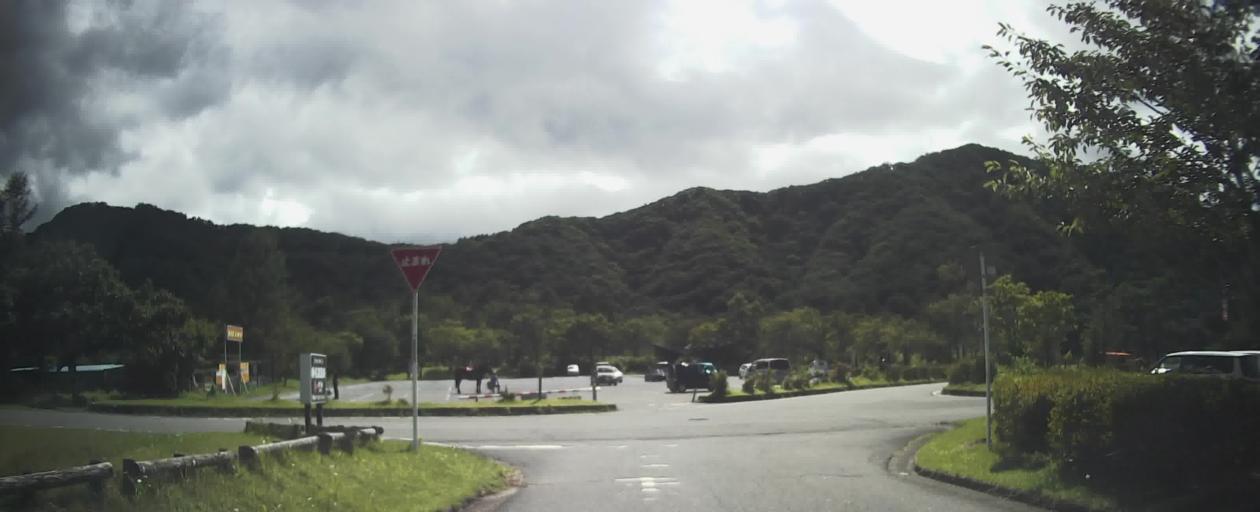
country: JP
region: Gunma
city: Nakanojomachi
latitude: 36.4713
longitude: 138.8742
